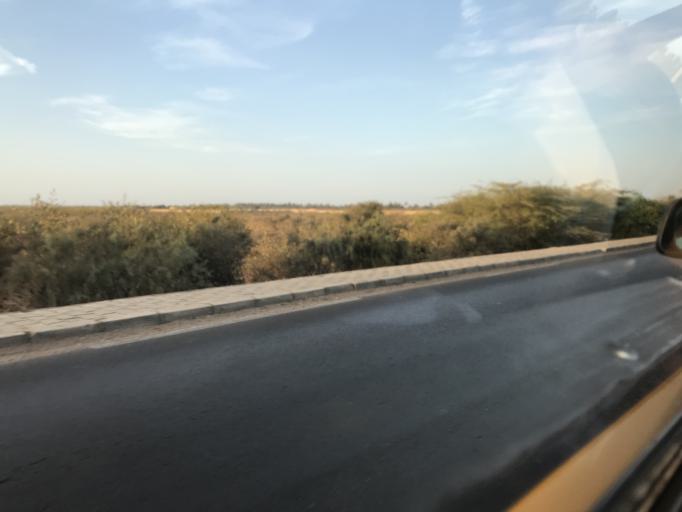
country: SN
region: Saint-Louis
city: Saint-Louis
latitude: 16.0374
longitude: -16.4642
